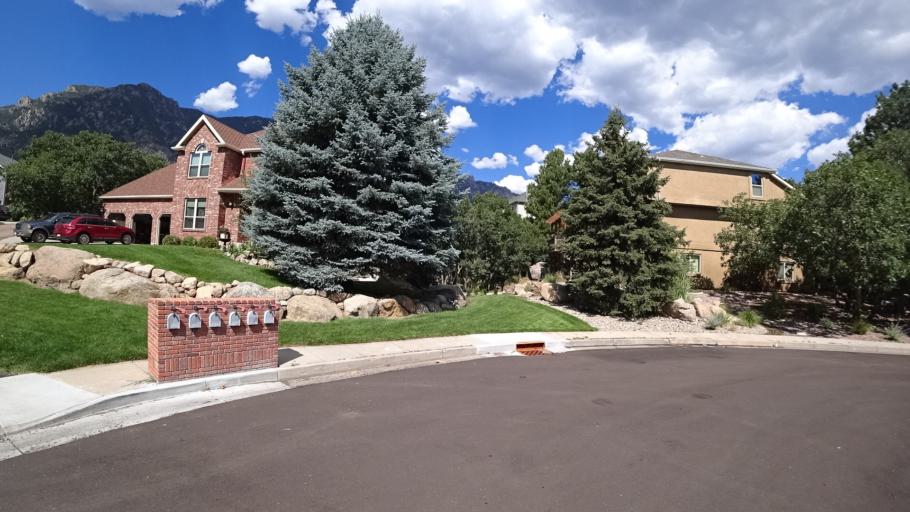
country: US
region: Colorado
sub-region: El Paso County
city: Fort Carson
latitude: 38.7487
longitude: -104.8318
